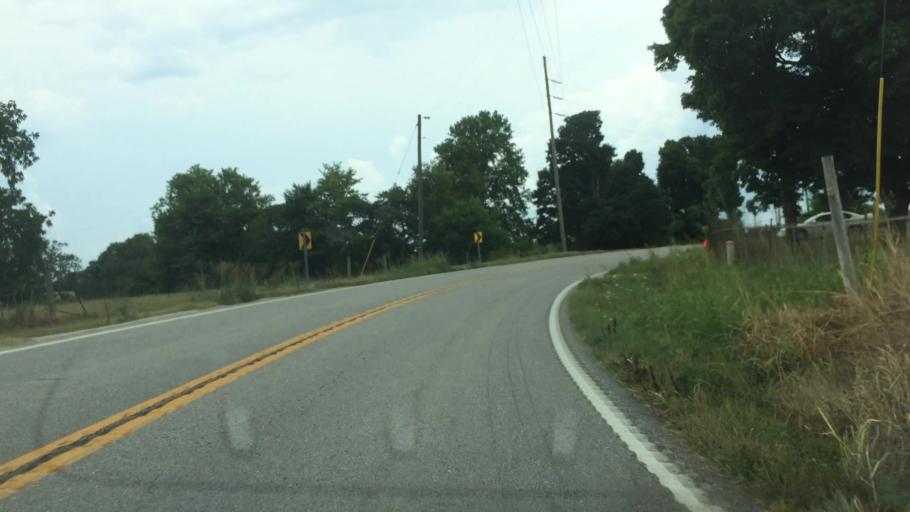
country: US
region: Missouri
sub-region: Greene County
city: Strafford
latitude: 37.2528
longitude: -93.1356
